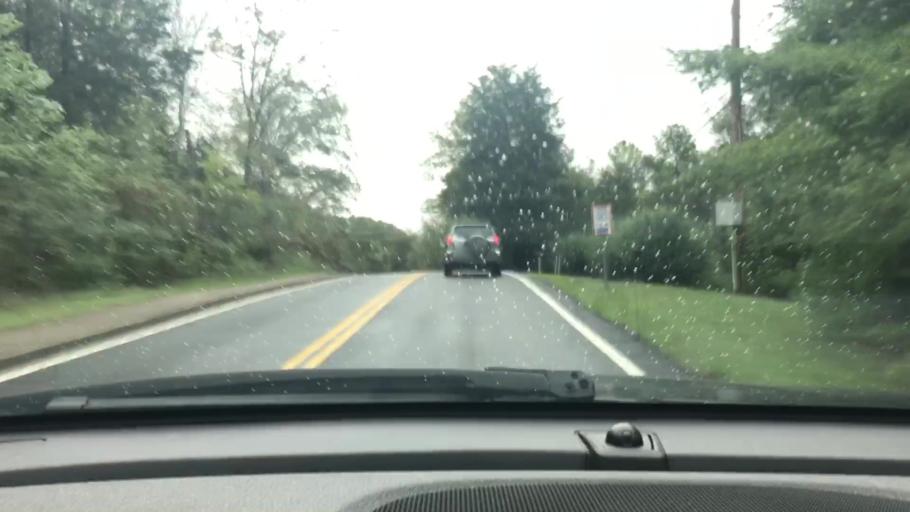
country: US
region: Tennessee
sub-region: Cheatham County
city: Kingston Springs
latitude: 36.0917
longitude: -87.1107
